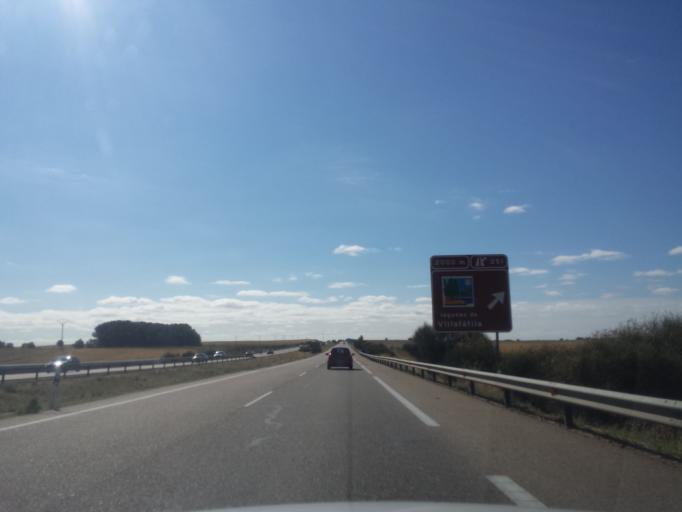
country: ES
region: Castille and Leon
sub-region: Provincia de Zamora
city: San Esteban del Molar
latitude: 41.9561
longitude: -5.5759
